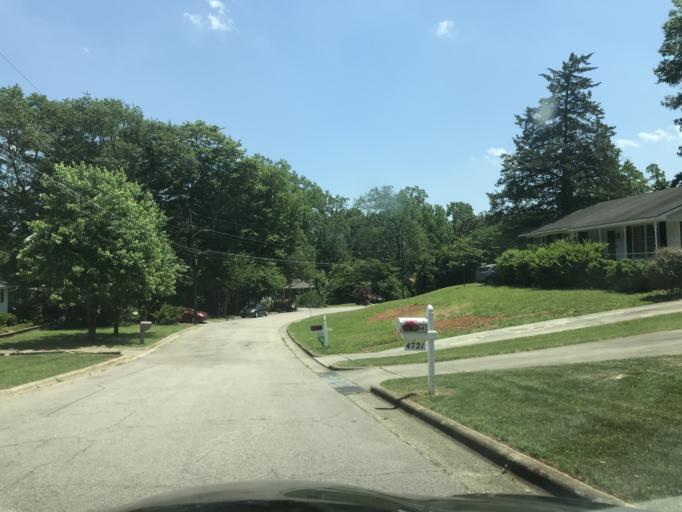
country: US
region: North Carolina
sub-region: Wake County
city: West Raleigh
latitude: 35.8443
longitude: -78.6329
